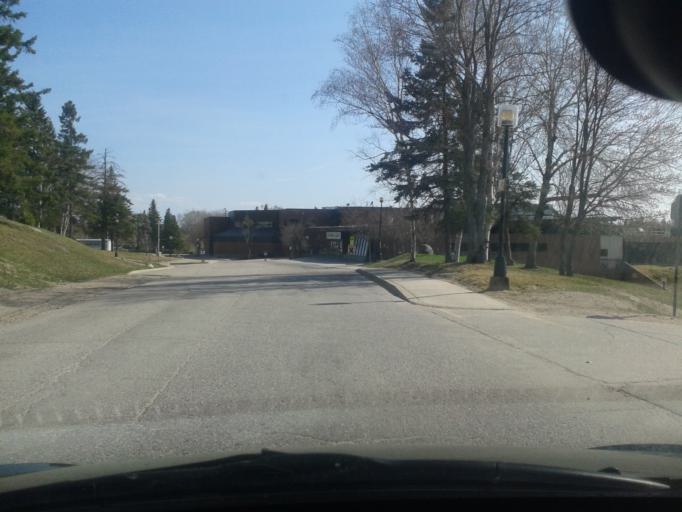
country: CA
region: Ontario
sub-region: Nipissing District
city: North Bay
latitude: 46.3445
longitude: -79.4915
